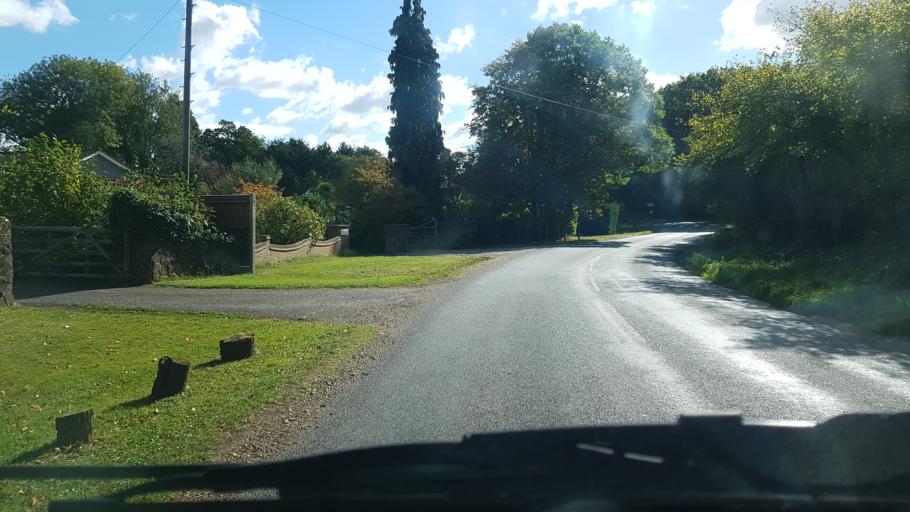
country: GB
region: England
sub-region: West Sussex
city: Rudgwick
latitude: 51.0673
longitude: -0.5428
